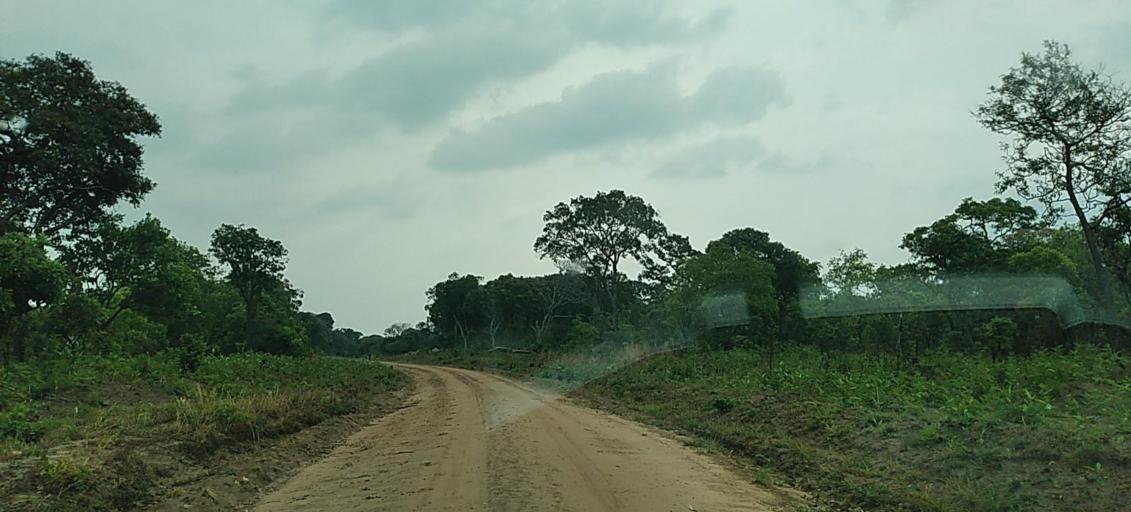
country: ZM
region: North-Western
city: Mwinilunga
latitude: -11.4188
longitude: 24.6001
